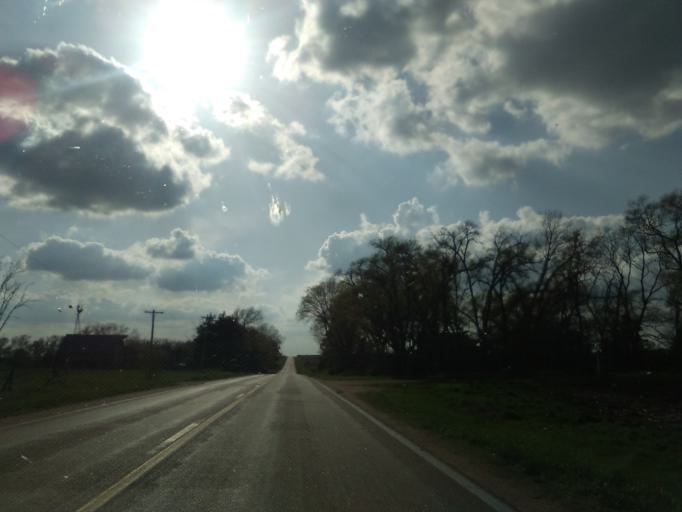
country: US
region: Nebraska
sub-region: Webster County
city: Red Cloud
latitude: 40.0889
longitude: -98.5465
